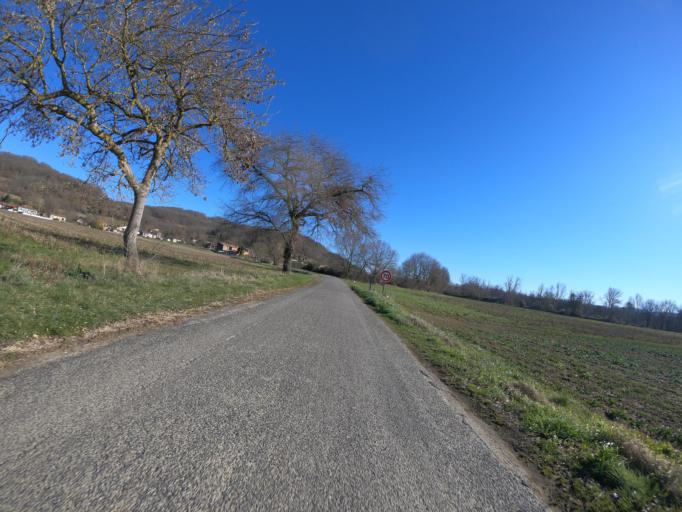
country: FR
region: Midi-Pyrenees
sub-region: Departement de l'Ariege
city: La Tour-du-Crieu
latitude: 43.0963
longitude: 1.7556
